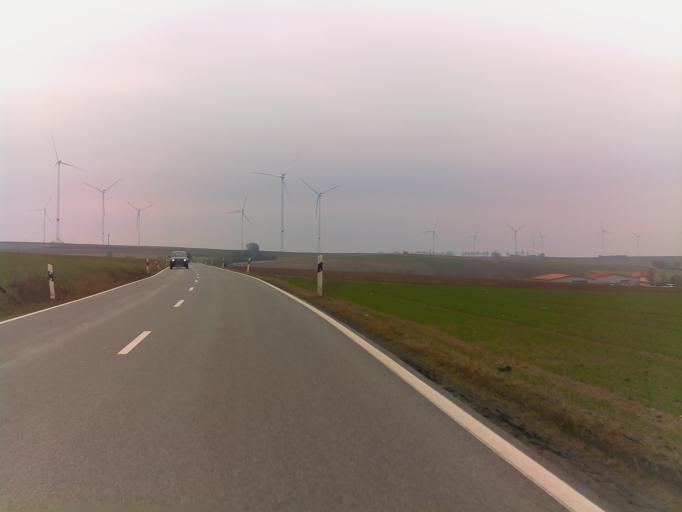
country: DE
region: Rheinland-Pfalz
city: Stetten
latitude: 49.6722
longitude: 8.0816
